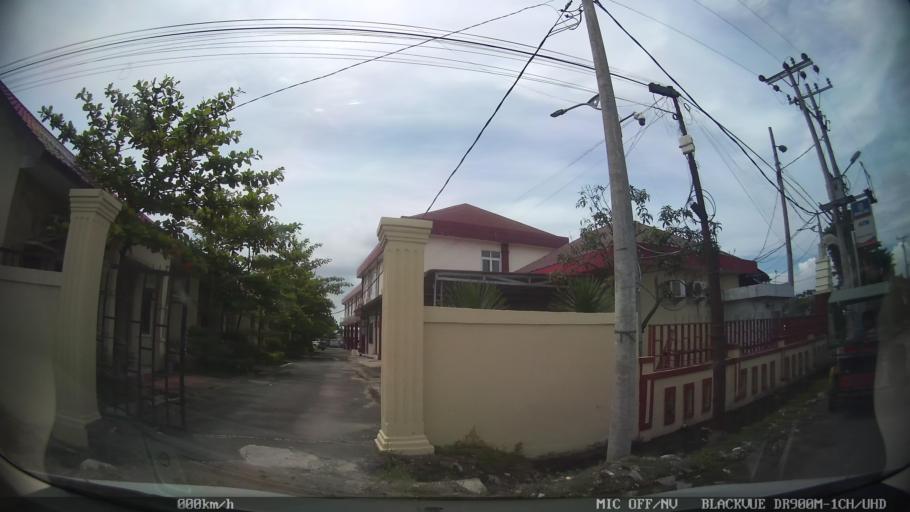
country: ID
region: North Sumatra
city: Belawan
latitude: 3.7786
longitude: 98.7036
